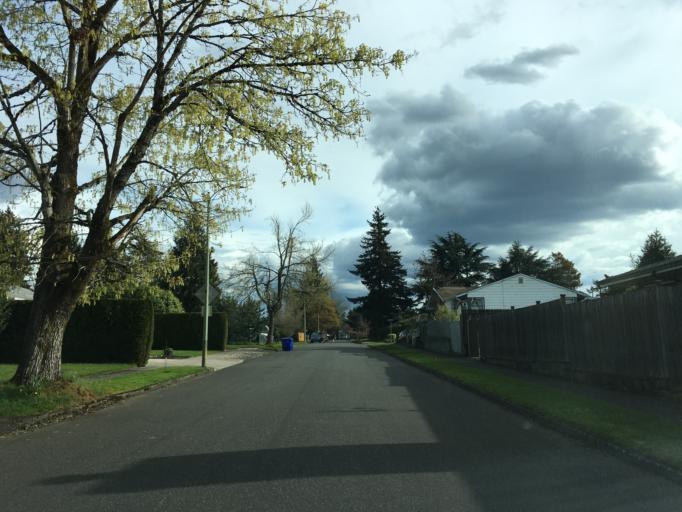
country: US
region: Oregon
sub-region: Multnomah County
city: Lents
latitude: 45.5444
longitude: -122.5387
